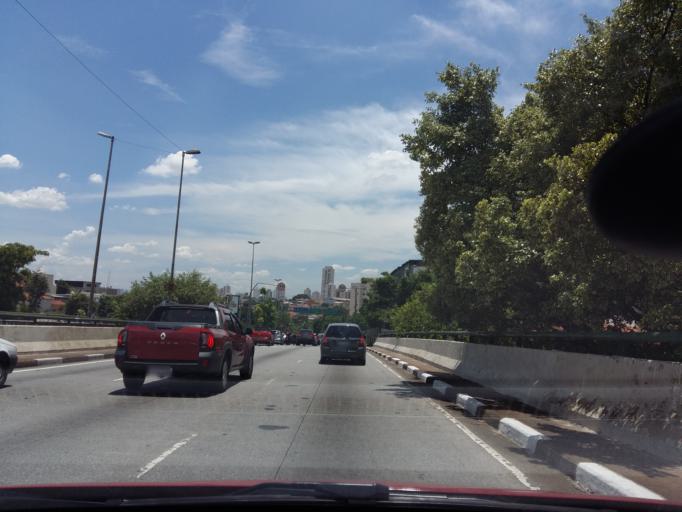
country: BR
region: Sao Paulo
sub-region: Diadema
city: Diadema
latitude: -23.6256
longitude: -46.6151
